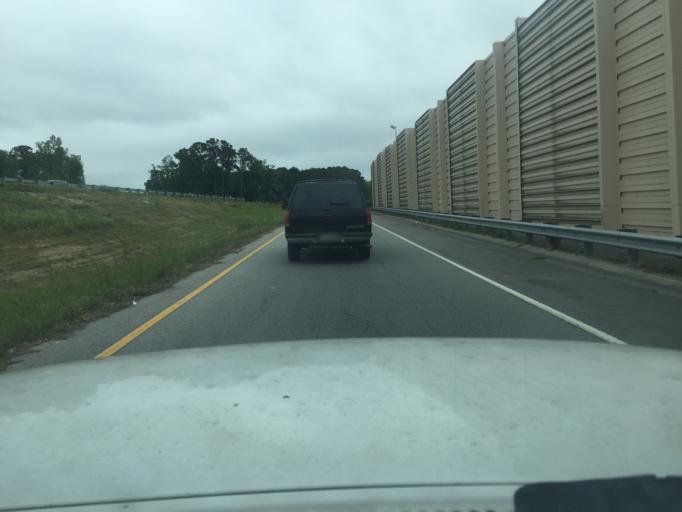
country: US
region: Georgia
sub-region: Chatham County
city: Montgomery
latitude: 31.9731
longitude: -81.1039
